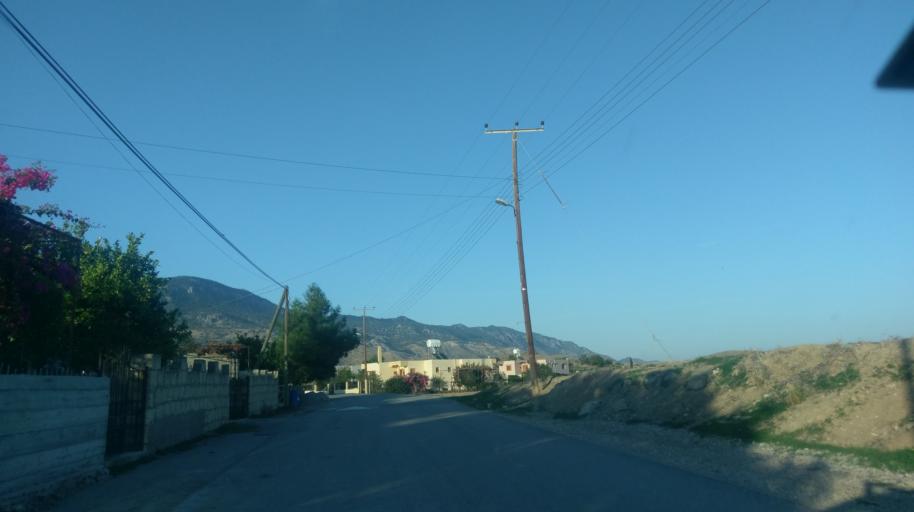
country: CY
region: Ammochostos
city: Lefkonoiko
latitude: 35.2542
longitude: 33.5494
